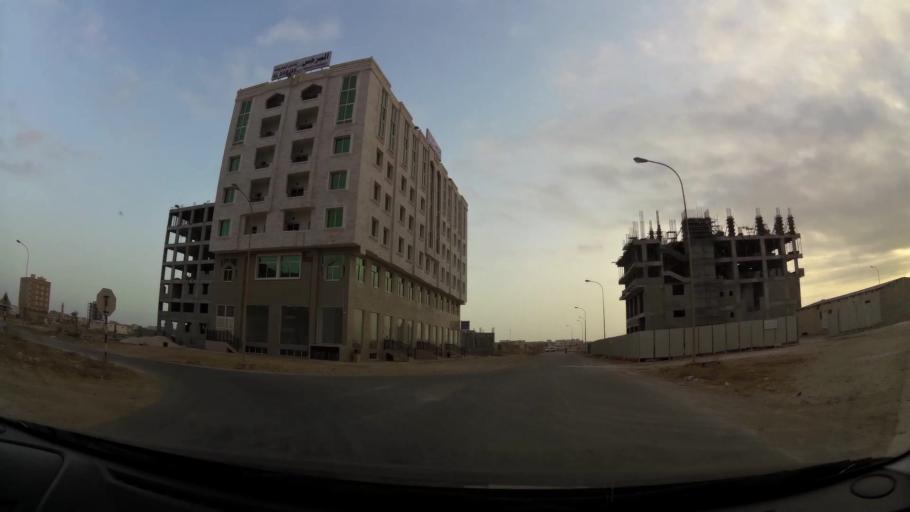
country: OM
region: Zufar
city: Salalah
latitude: 17.0278
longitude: 54.0285
